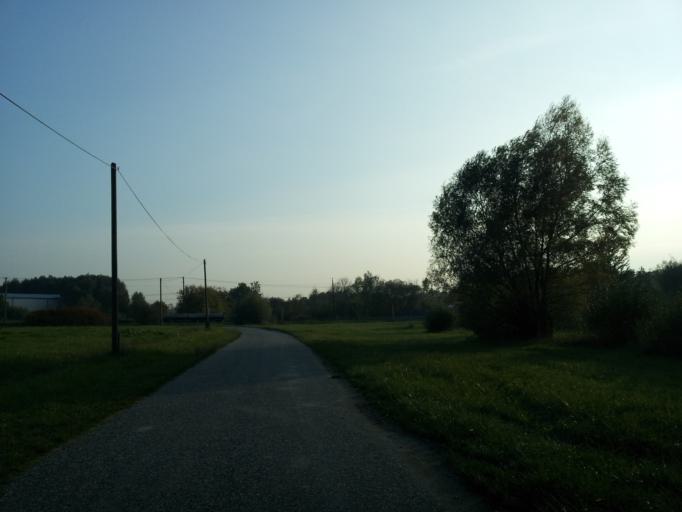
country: HU
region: Komarom-Esztergom
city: Kisber
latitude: 47.5105
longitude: 18.0090
